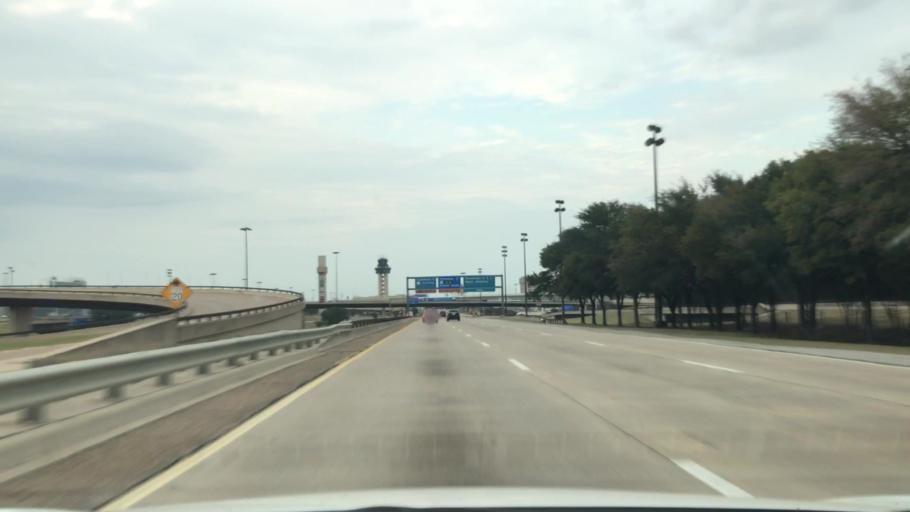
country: US
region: Texas
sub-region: Tarrant County
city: Grapevine
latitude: 32.8883
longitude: -97.0399
